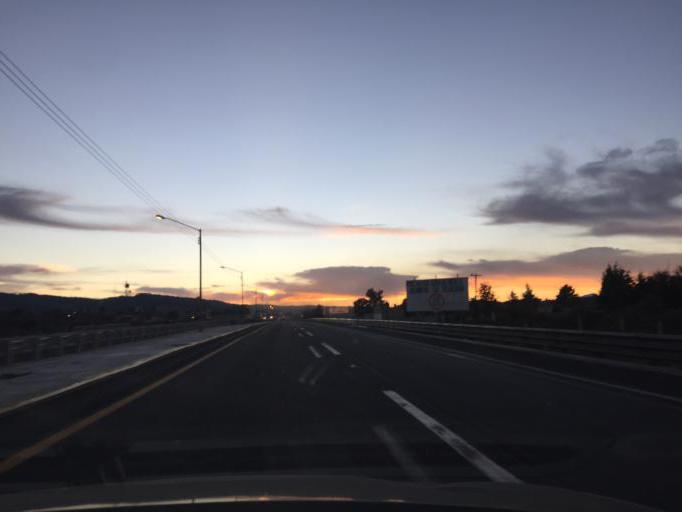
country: MX
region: Puebla
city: San Jose Esperanza
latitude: 18.8655
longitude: -97.3746
